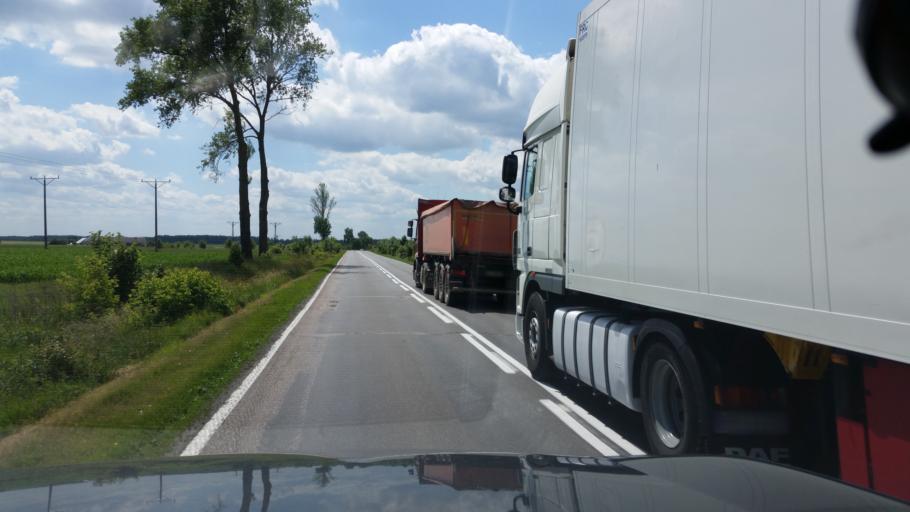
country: PL
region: Podlasie
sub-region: Powiat lomzynski
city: Sniadowo
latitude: 53.0772
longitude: 22.0170
